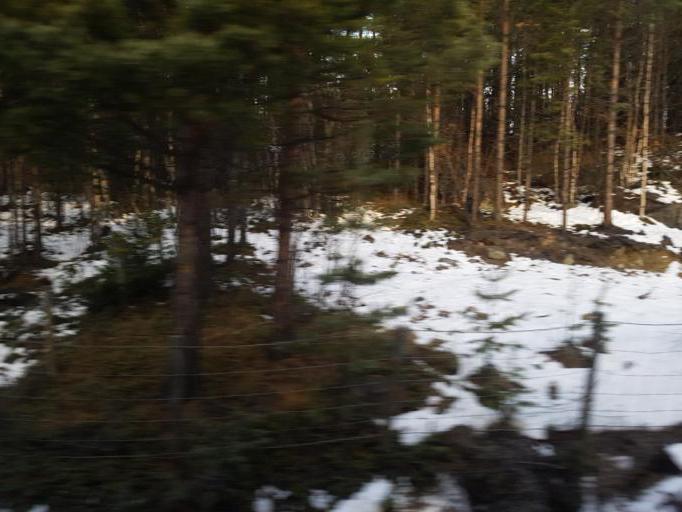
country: NO
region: Sor-Trondelag
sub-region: Rennebu
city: Berkak
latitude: 62.6757
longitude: 9.9176
